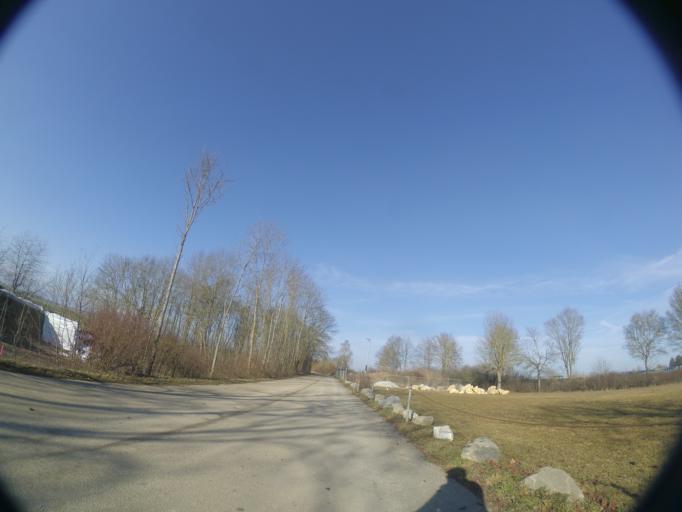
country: DE
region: Baden-Wuerttemberg
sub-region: Tuebingen Region
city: Dornstadt
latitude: 48.4742
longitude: 9.9396
